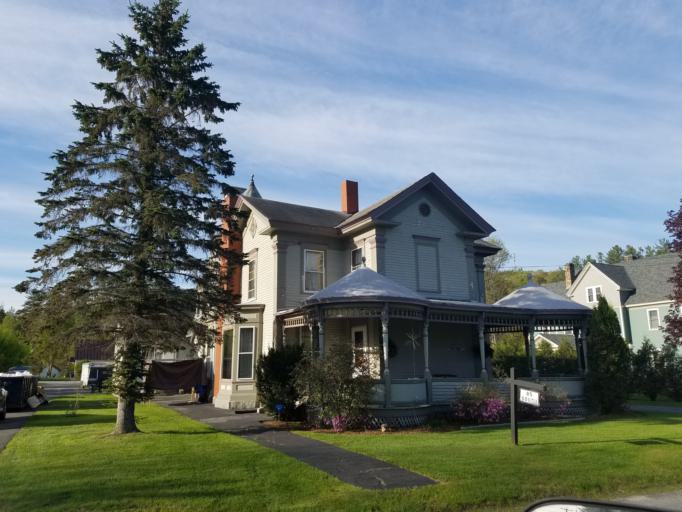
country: US
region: New Hampshire
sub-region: Grafton County
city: Littleton
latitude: 44.3036
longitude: -71.7729
